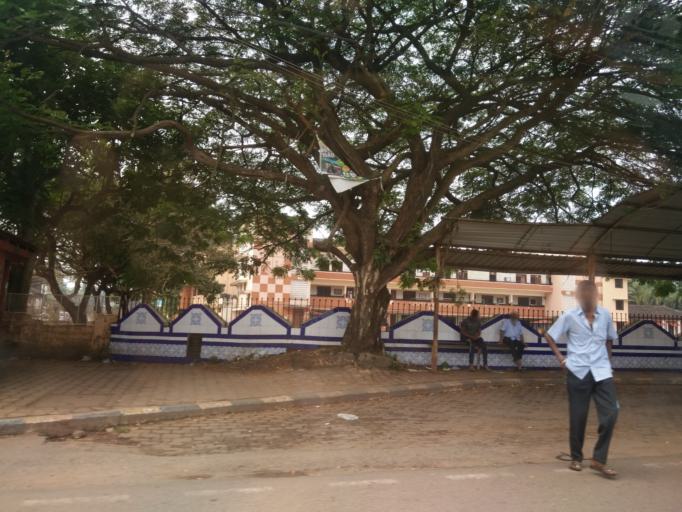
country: IN
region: Goa
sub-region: South Goa
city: Madgaon
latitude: 15.2564
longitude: 73.9665
